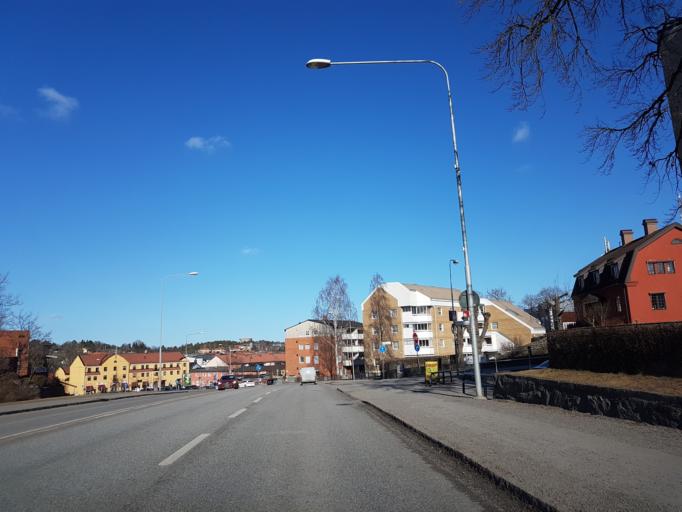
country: SE
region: Stockholm
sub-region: Norrtalje Kommun
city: Norrtalje
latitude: 59.7554
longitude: 18.6966
